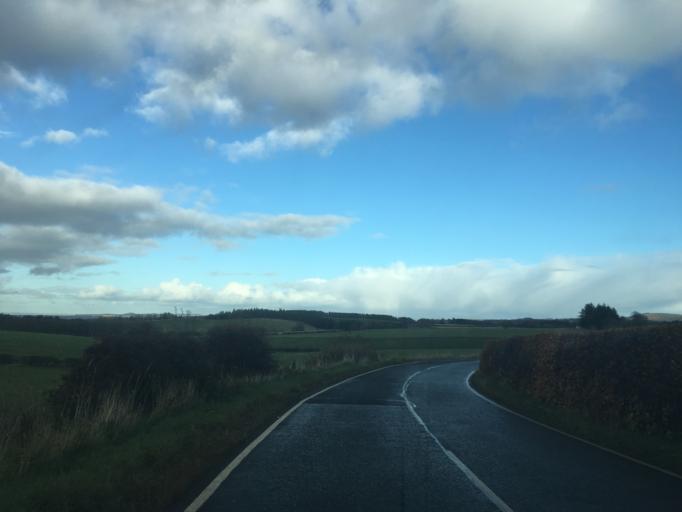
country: GB
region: Scotland
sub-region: East Lothian
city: Pencaitland
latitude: 55.8401
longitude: -2.8938
